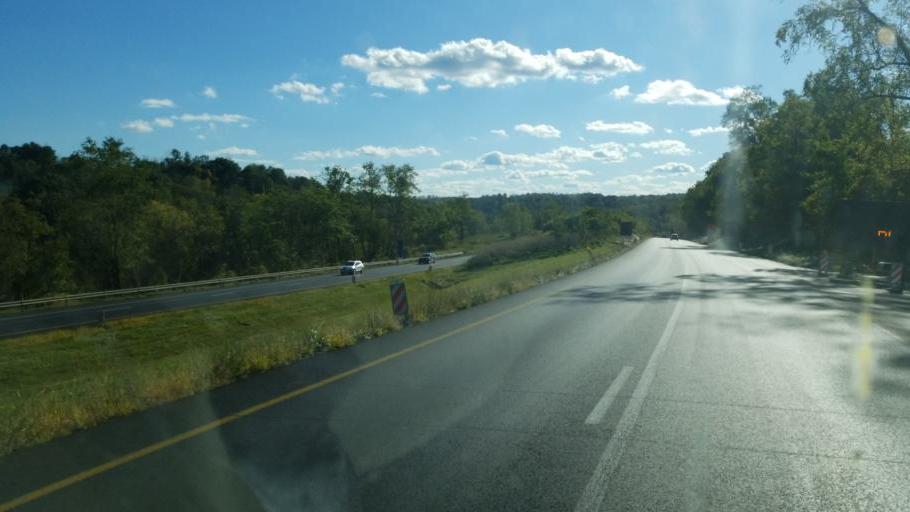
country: US
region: Pennsylvania
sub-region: Washington County
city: Wolfdale
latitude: 40.1299
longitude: -80.3582
